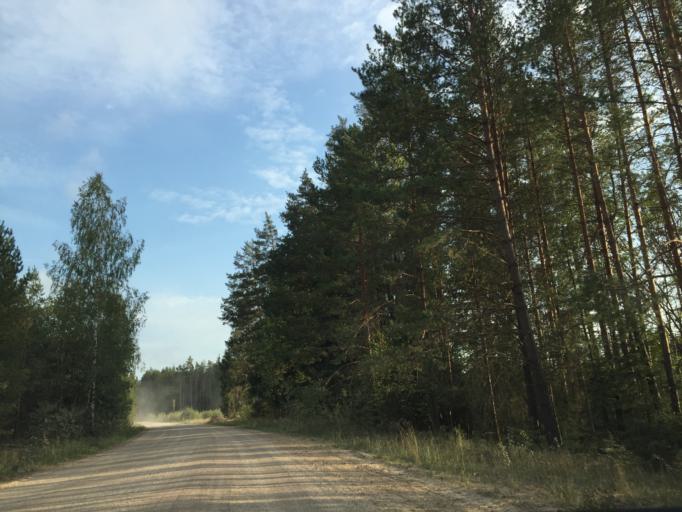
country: LV
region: Baldone
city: Baldone
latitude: 56.7921
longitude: 24.4398
